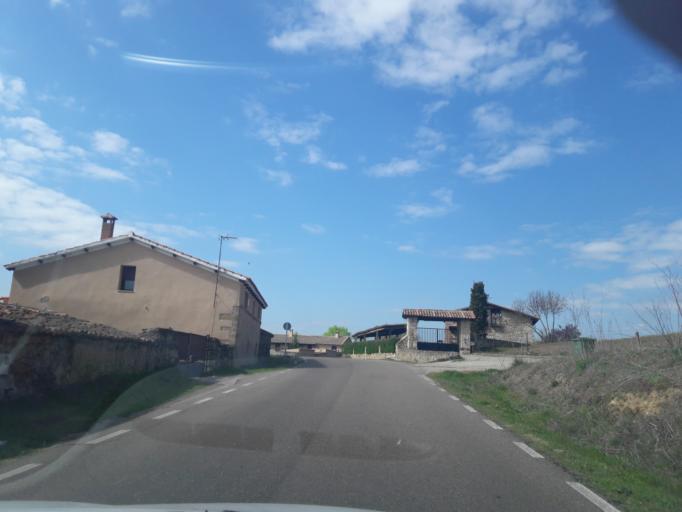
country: ES
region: Castille and Leon
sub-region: Provincia de Salamanca
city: Zamarra
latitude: 40.5676
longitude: -6.4764
